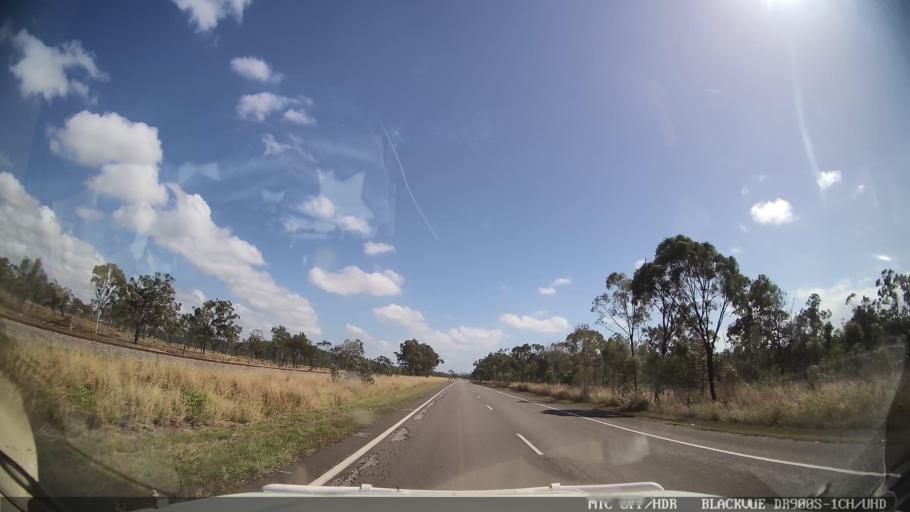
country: AU
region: Queensland
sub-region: Whitsunday
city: Red Hill
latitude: -20.1861
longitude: 148.3563
